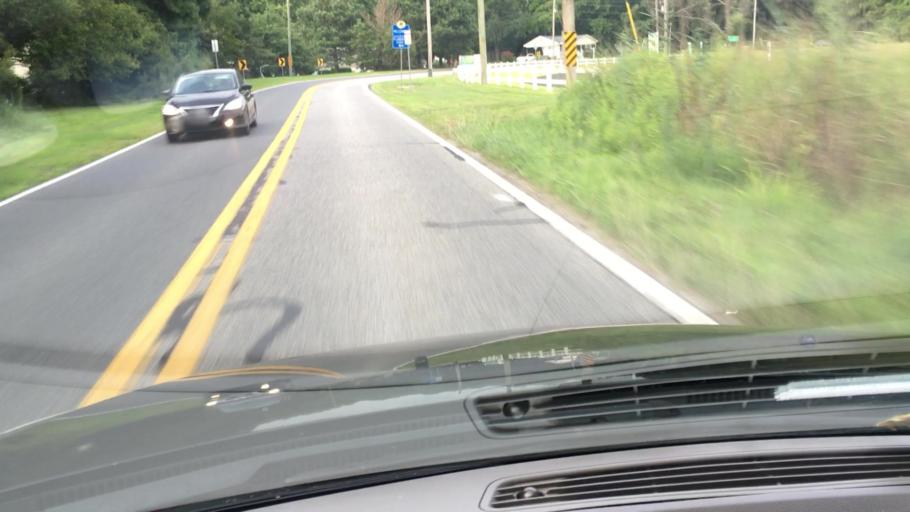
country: US
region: Delaware
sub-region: Sussex County
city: Ocean View
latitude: 38.5121
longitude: -75.1078
